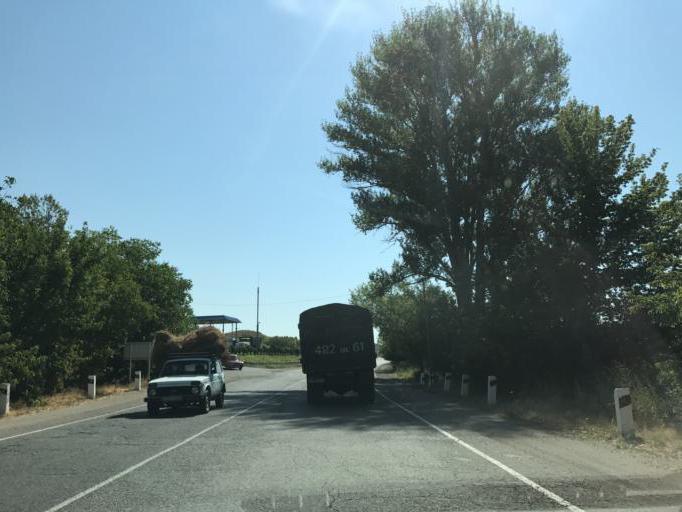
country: AM
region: Vayots' Dzori Marz
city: Getap'
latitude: 39.7485
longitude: 45.3125
